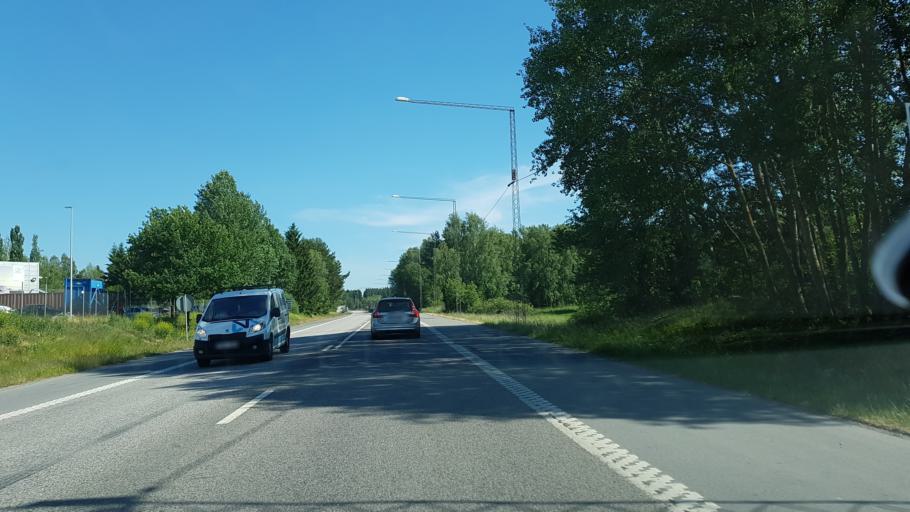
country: SE
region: Stockholm
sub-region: Sigtuna Kommun
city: Rosersberg
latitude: 59.6089
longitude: 17.8901
